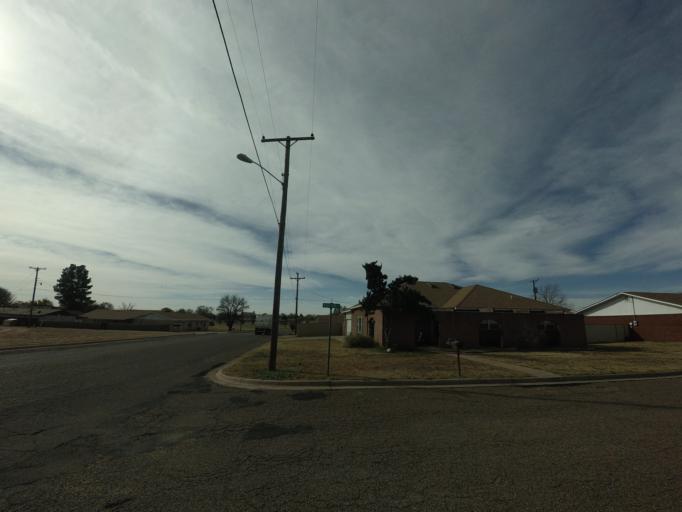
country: US
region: New Mexico
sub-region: Curry County
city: Clovis
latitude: 34.4139
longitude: -103.1912
